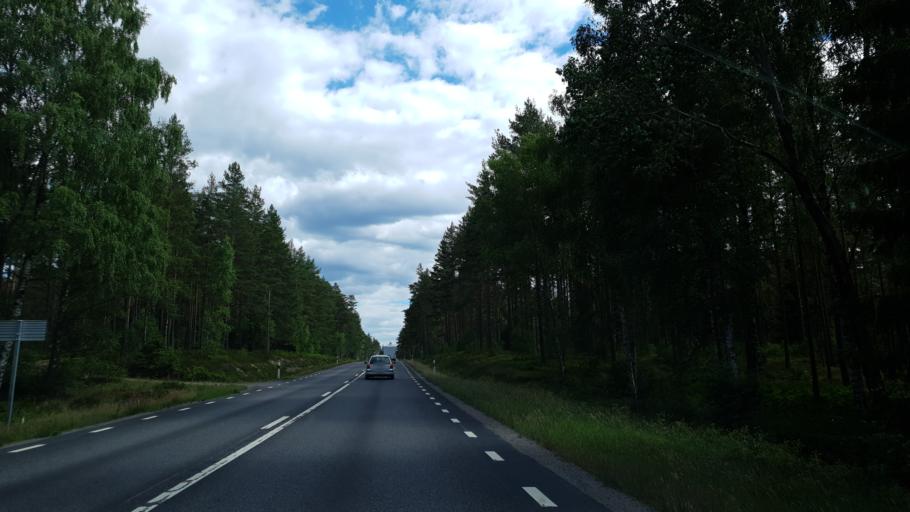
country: SE
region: Kronoberg
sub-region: Lessebo Kommun
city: Lessebo
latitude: 56.8221
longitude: 15.4067
